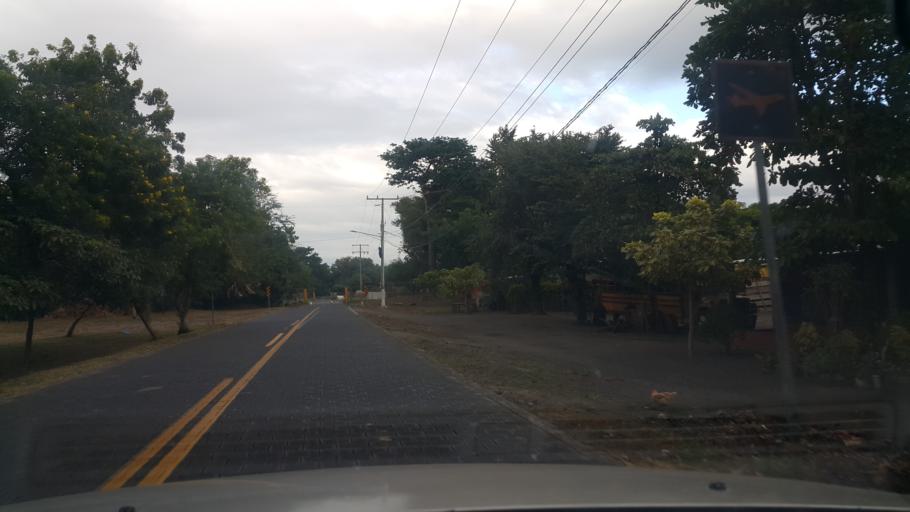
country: NI
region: Rivas
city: Moyogalpa
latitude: 11.5219
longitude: -85.7038
